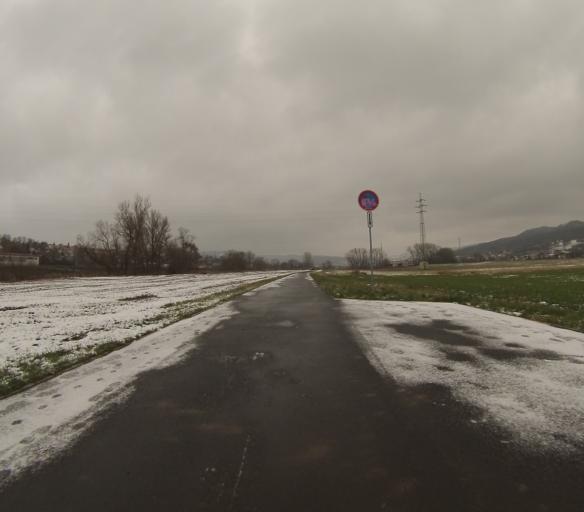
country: CZ
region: Ustecky
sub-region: Okres Decin
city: Decin
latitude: 50.7500
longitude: 14.1859
